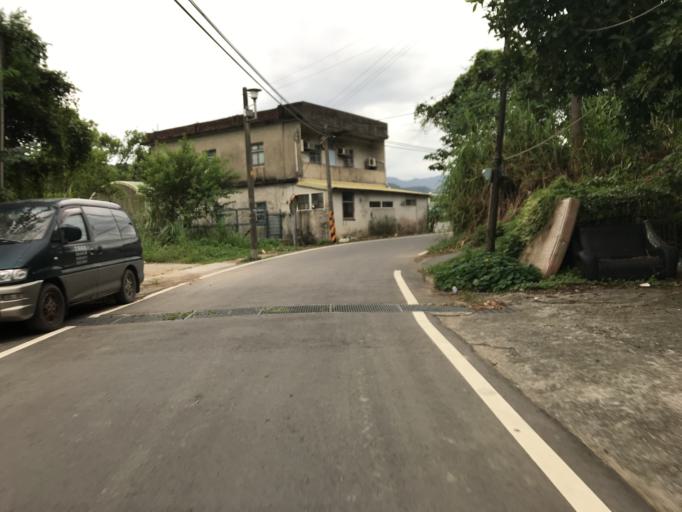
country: TW
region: Taiwan
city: Daxi
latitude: 24.7841
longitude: 121.1755
